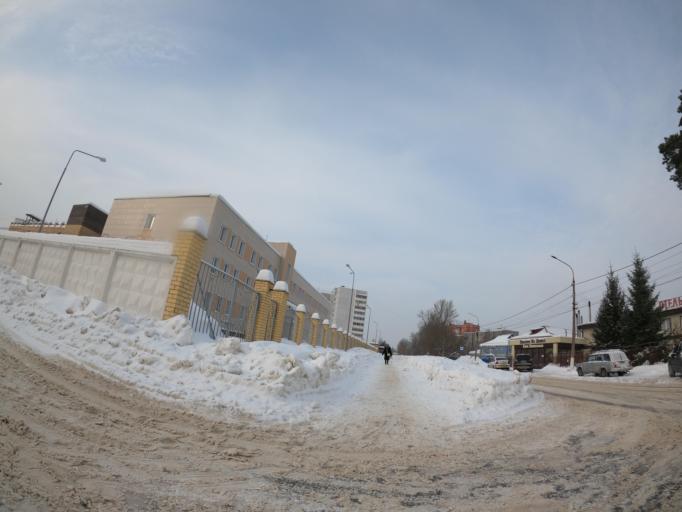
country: RU
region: Moskovskaya
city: Elektrogorsk
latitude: 55.8867
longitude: 38.7777
